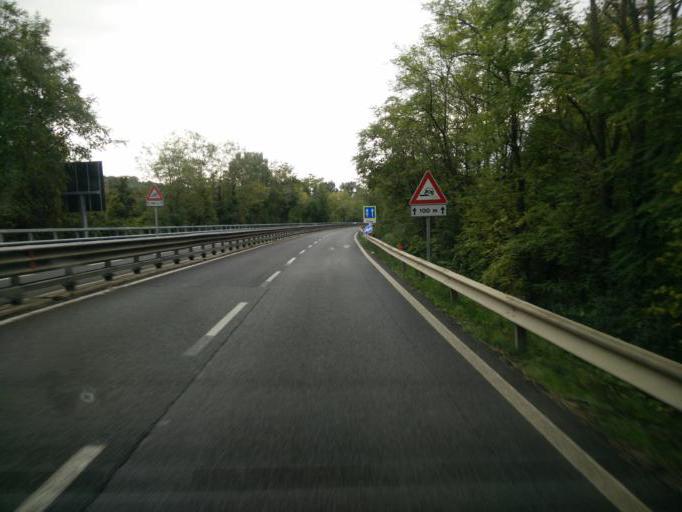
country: IT
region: Tuscany
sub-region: Province of Florence
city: Sambuca
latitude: 43.5978
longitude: 11.1946
